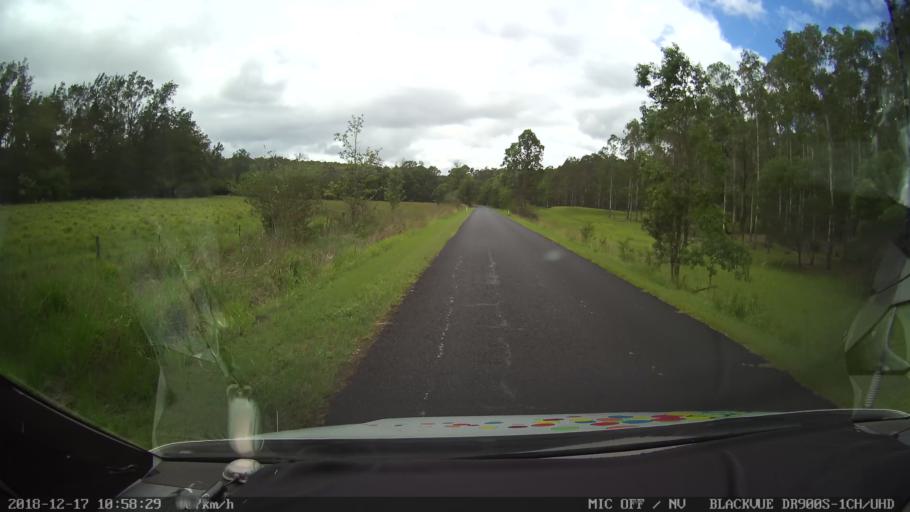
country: AU
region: New South Wales
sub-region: Richmond Valley
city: Casino
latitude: -28.8243
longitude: 152.6050
